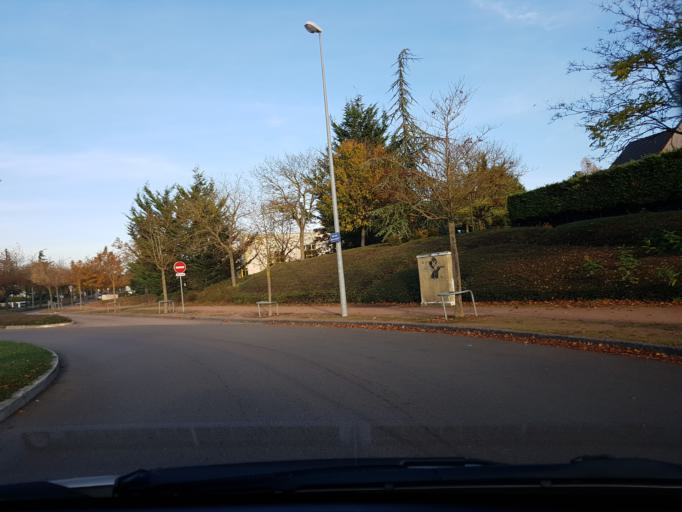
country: FR
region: Bourgogne
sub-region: Departement de la Cote-d'Or
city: Fontaine-les-Dijon
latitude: 47.3542
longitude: 5.0406
